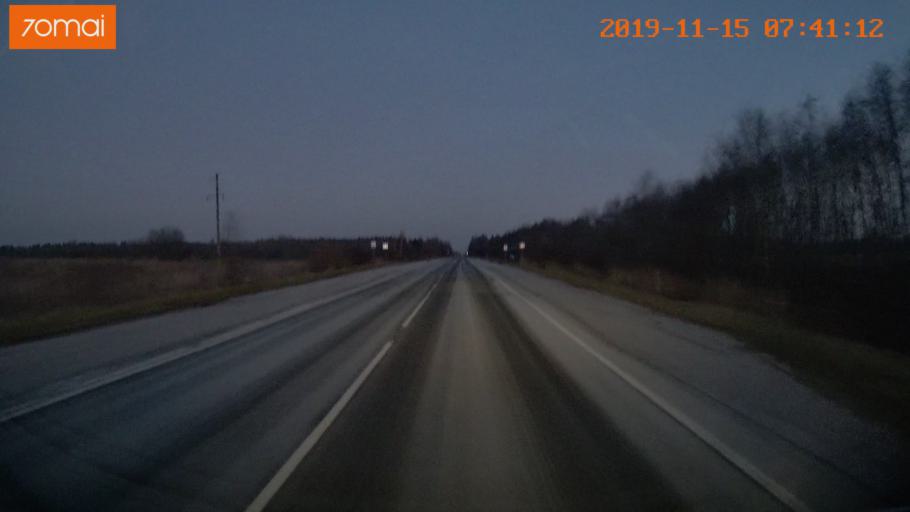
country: RU
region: Vologda
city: Sheksna
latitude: 58.7777
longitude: 38.3619
